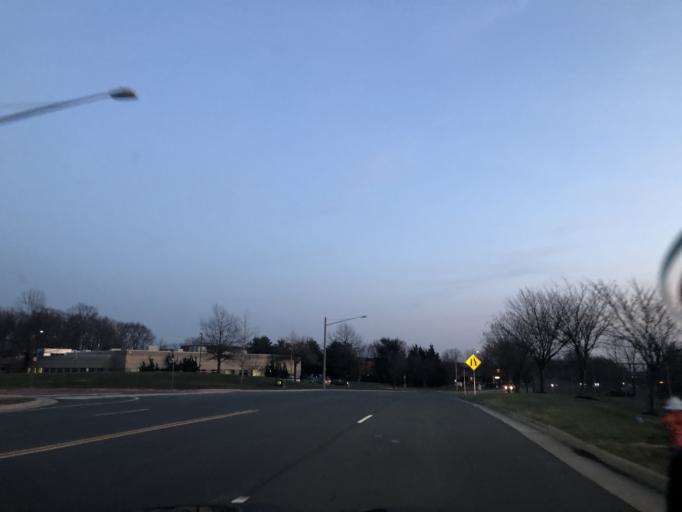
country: US
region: Virginia
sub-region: Loudoun County
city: Leesburg
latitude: 39.0849
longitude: -77.5572
